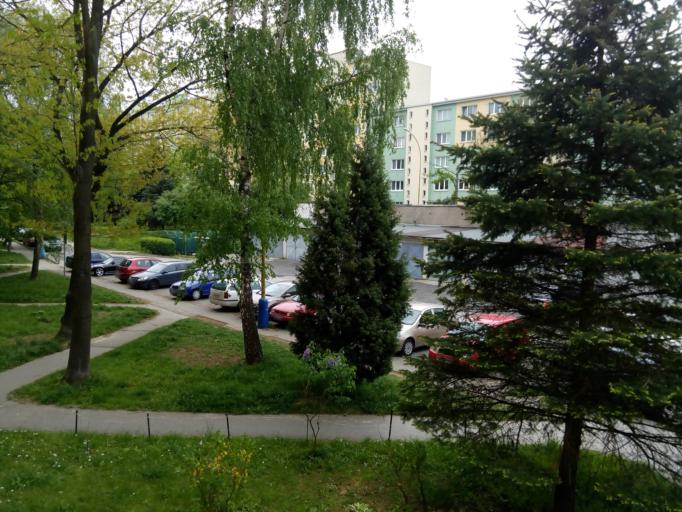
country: SK
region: Kosicky
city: Kosice
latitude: 48.7200
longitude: 21.2292
